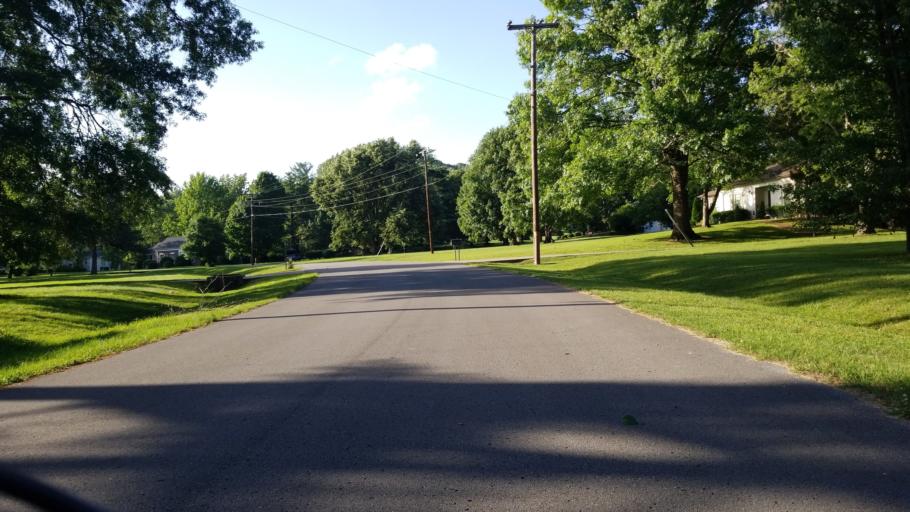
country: US
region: Tennessee
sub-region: Davidson County
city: Forest Hills
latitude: 36.0406
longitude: -86.8511
